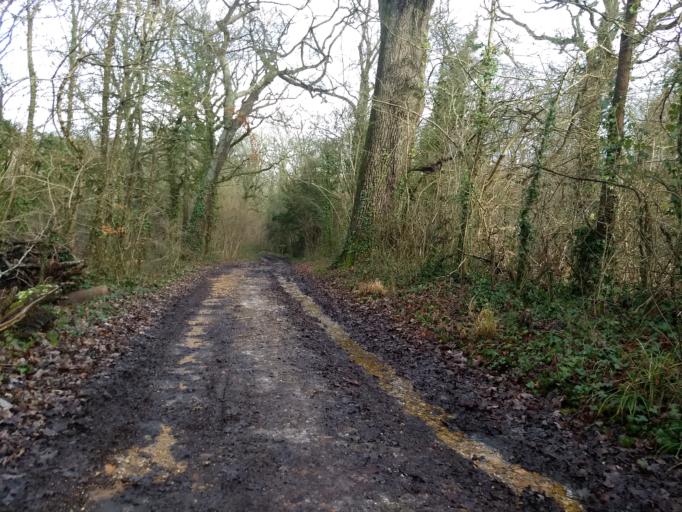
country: GB
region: England
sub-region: Isle of Wight
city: Newchurch
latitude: 50.7129
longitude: -1.2311
